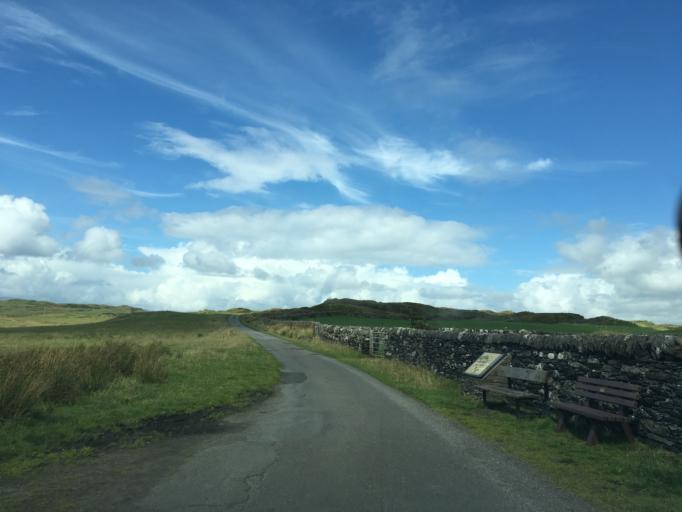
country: GB
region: Scotland
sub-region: Argyll and Bute
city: Oban
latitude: 56.2209
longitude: -5.6398
